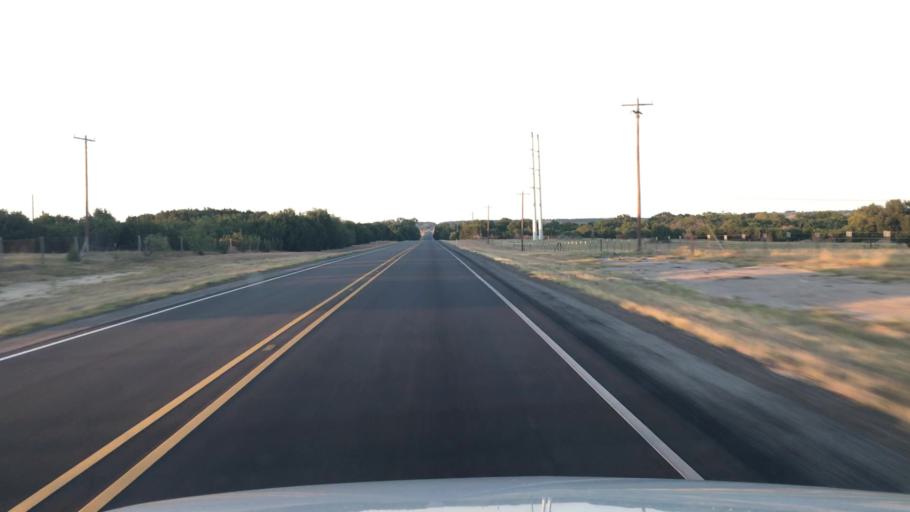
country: US
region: Texas
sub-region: Hamilton County
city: Hico
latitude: 32.0620
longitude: -97.9944
